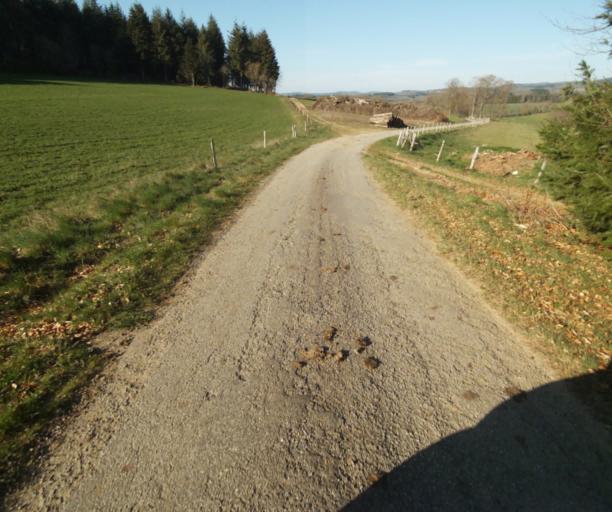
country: FR
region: Limousin
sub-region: Departement de la Correze
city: Chamboulive
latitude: 45.4788
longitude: 1.7275
